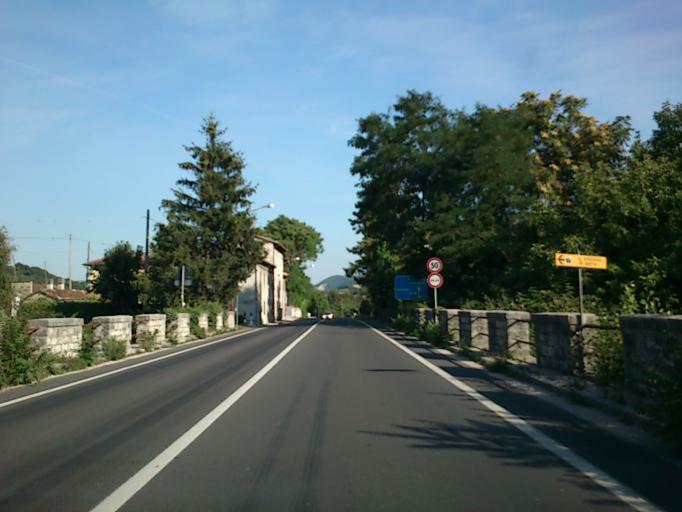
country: IT
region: The Marches
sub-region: Provincia di Pesaro e Urbino
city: Canavaccio
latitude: 43.6903
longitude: 12.7103
